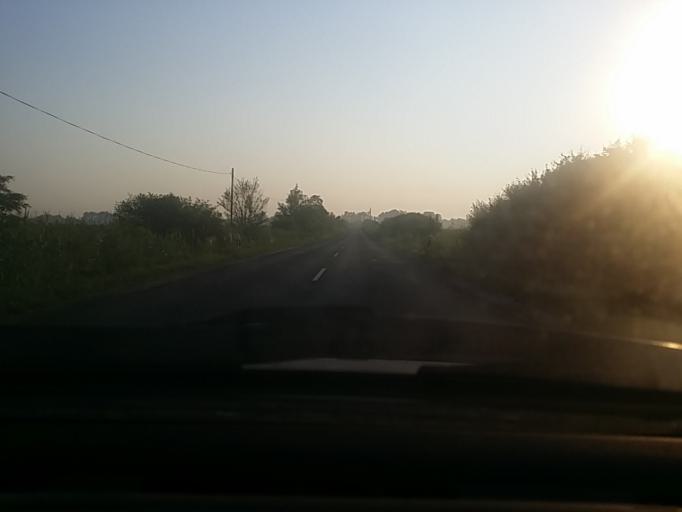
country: HU
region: Pest
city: Nagykata
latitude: 47.4339
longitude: 19.7712
